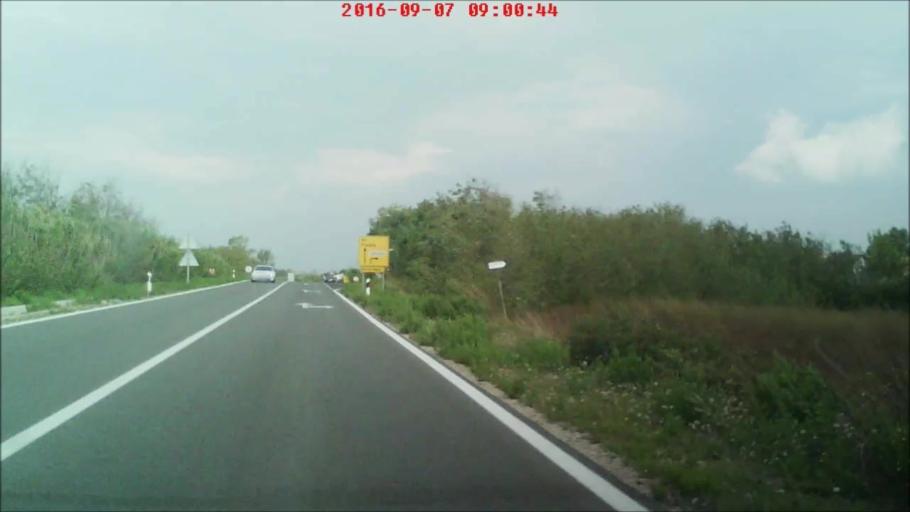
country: HR
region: Zadarska
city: Nin
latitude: 44.2519
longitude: 15.1611
